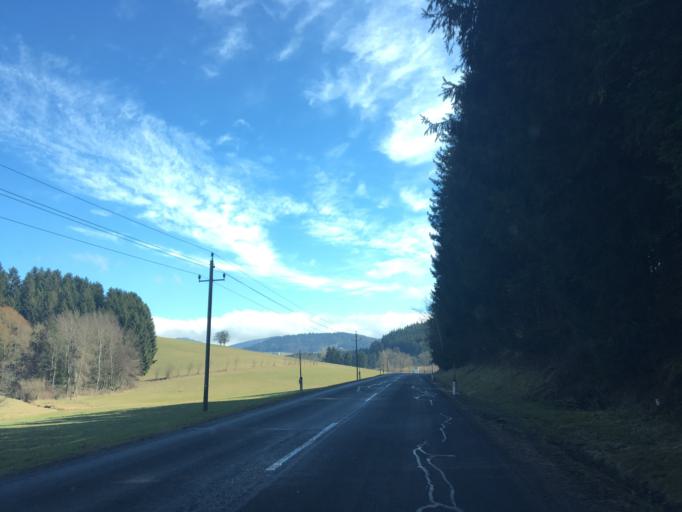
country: AT
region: Lower Austria
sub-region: Politischer Bezirk Melk
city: Dorfstetten
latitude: 48.2778
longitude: 14.9295
